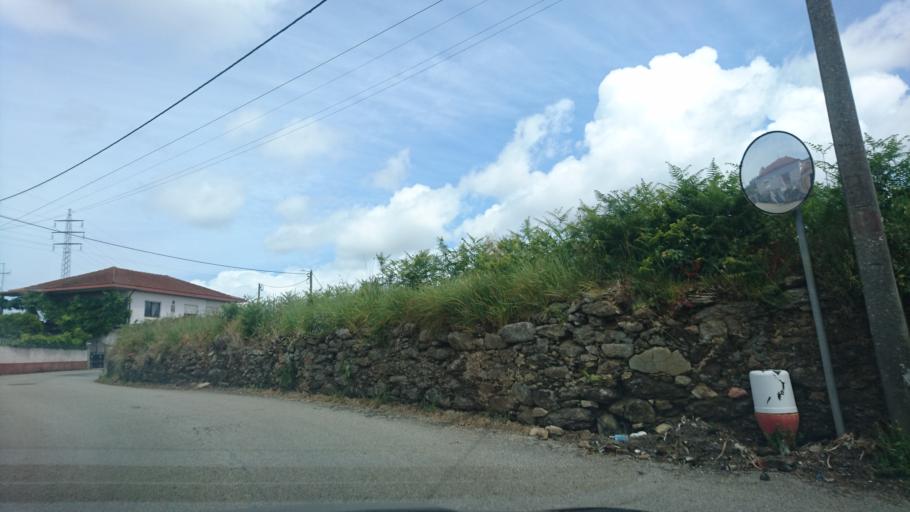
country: PT
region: Aveiro
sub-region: Santa Maria da Feira
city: Rio Meao
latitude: 40.9210
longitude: -8.5819
